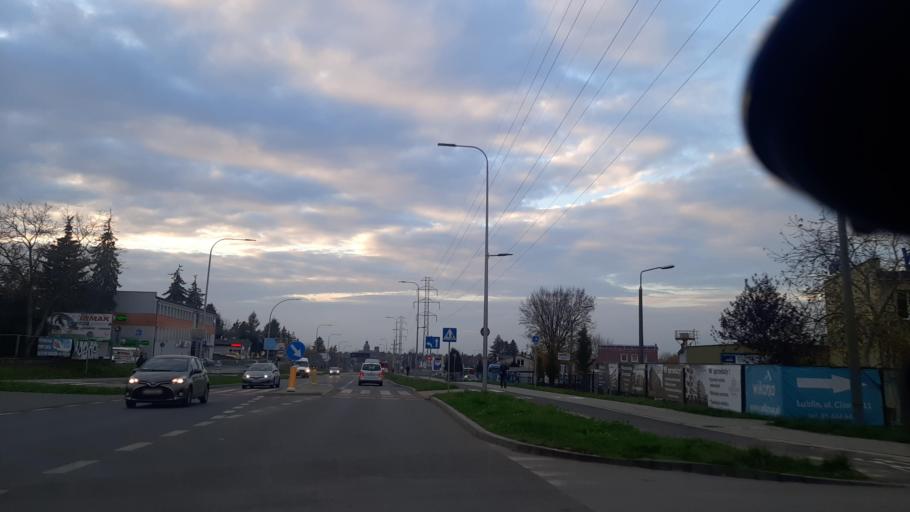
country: PL
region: Lublin Voivodeship
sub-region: Powiat lubelski
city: Lublin
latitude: 51.2502
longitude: 22.5126
